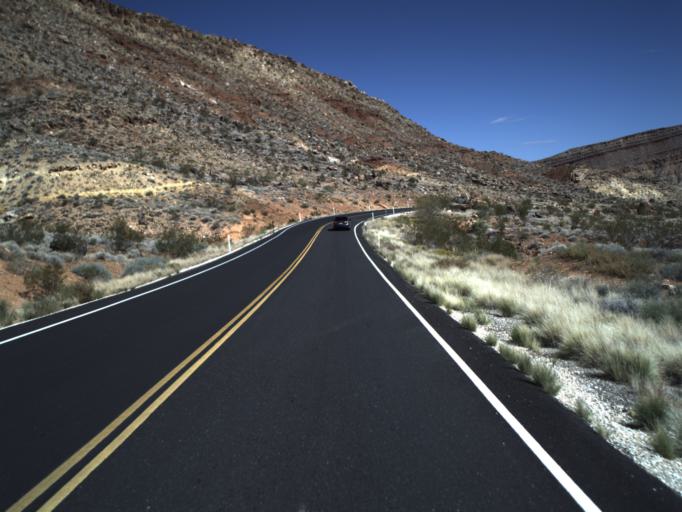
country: US
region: Utah
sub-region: Washington County
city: Hurricane
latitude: 37.1851
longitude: -113.3976
